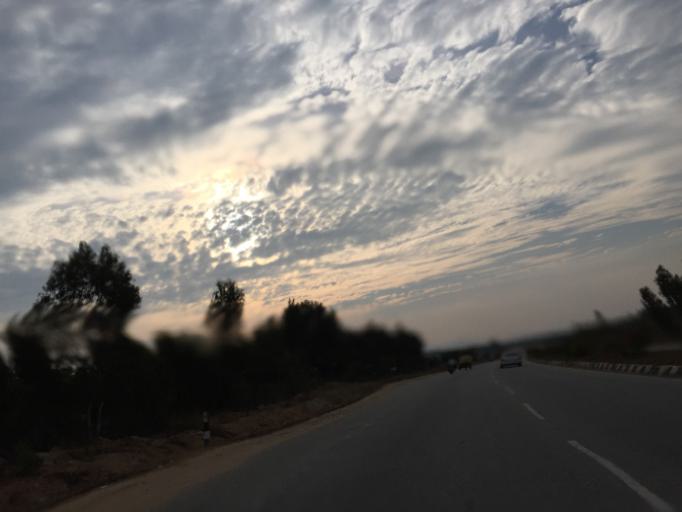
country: IN
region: Karnataka
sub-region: Kolar
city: Mulbagal
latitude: 13.1460
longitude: 78.2811
